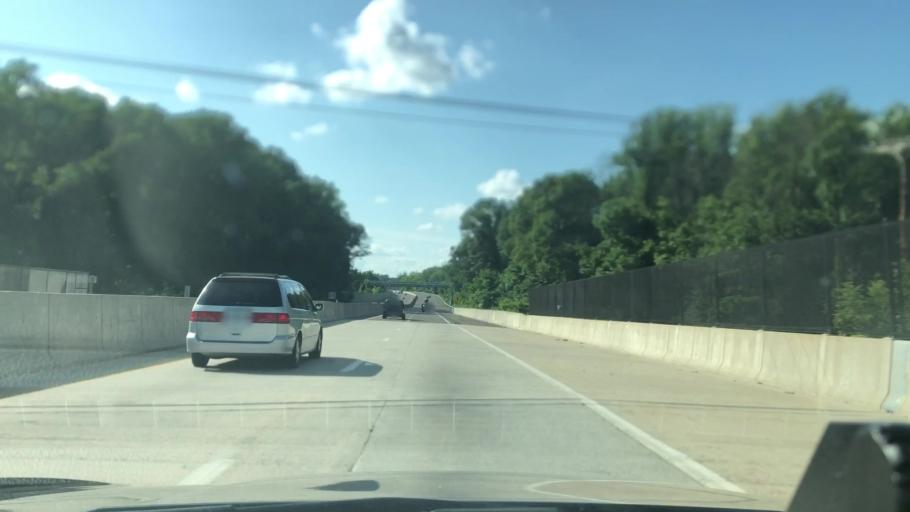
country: US
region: Pennsylvania
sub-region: Montgomery County
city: Ambler
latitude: 40.1668
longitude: -75.2041
